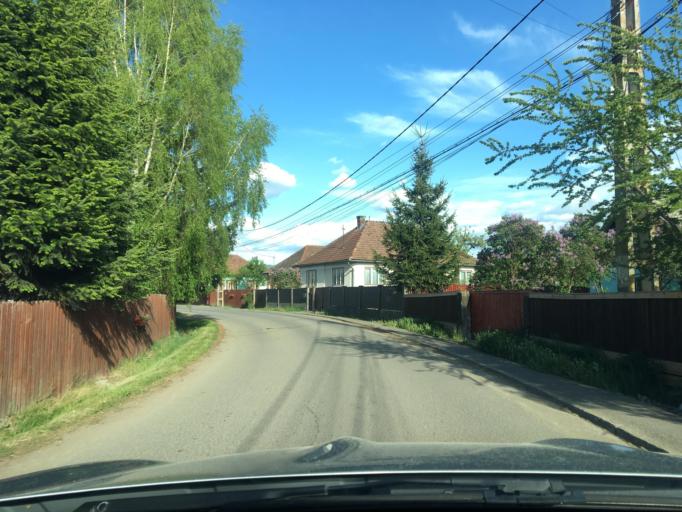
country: RO
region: Harghita
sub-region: Comuna Ditrau
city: Ditrau
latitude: 46.7993
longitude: 25.4912
